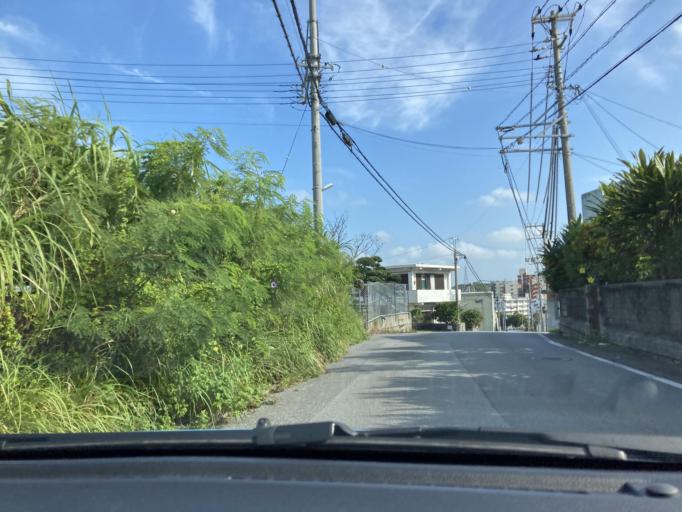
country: JP
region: Okinawa
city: Ginowan
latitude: 26.2342
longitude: 127.7448
